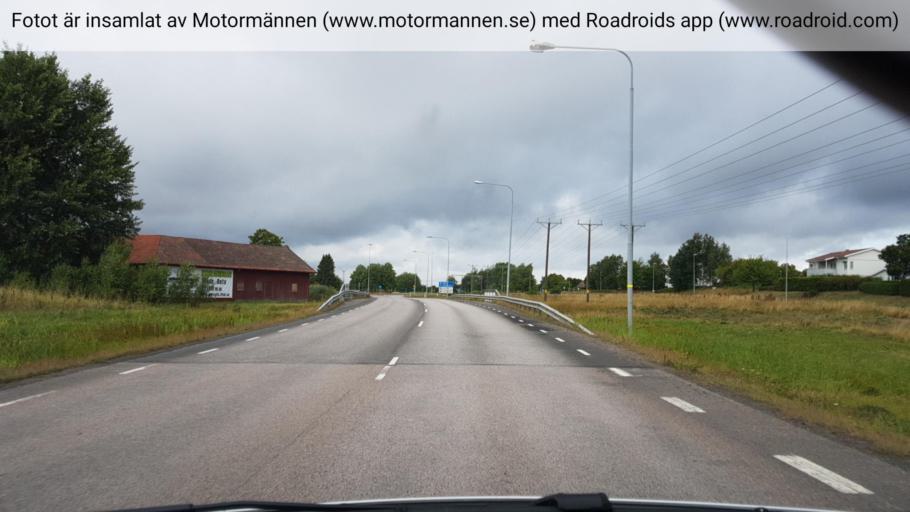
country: SE
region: Vaestra Goetaland
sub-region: Skara Kommun
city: Skara
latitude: 58.3937
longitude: 13.4570
